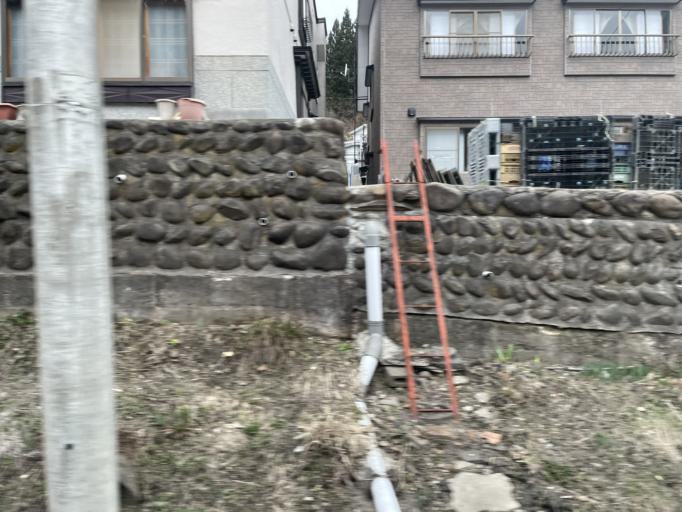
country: JP
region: Aomori
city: Namioka
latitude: 40.7883
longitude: 140.6323
